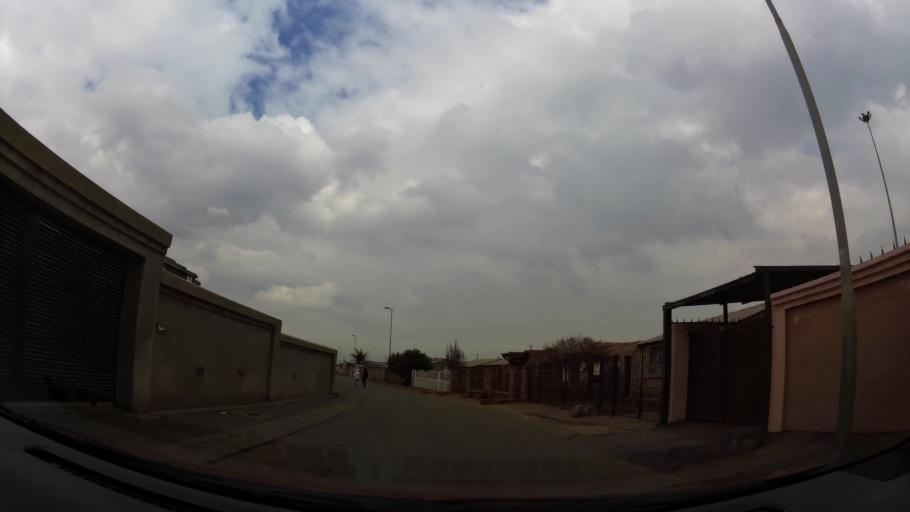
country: ZA
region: Gauteng
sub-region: City of Johannesburg Metropolitan Municipality
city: Soweto
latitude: -26.2626
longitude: 27.8314
